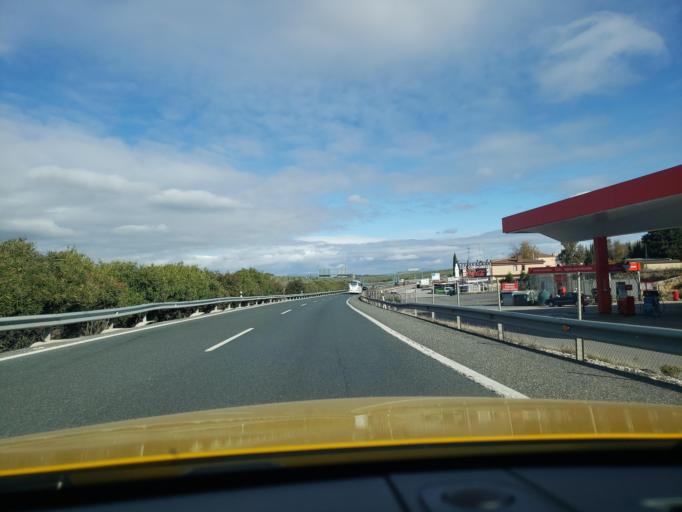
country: ES
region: Andalusia
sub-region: Provincia de Malaga
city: Villanueva de Tapia
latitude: 37.1331
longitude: -4.2852
